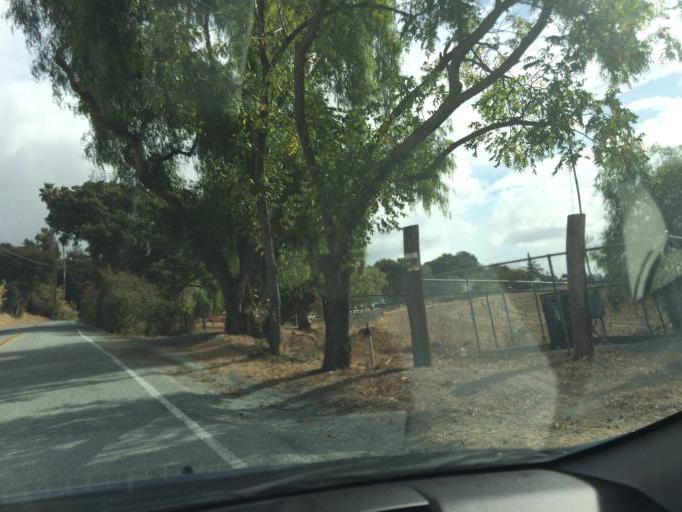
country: US
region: California
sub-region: Santa Clara County
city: Alum Rock
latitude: 37.3446
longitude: -121.7810
